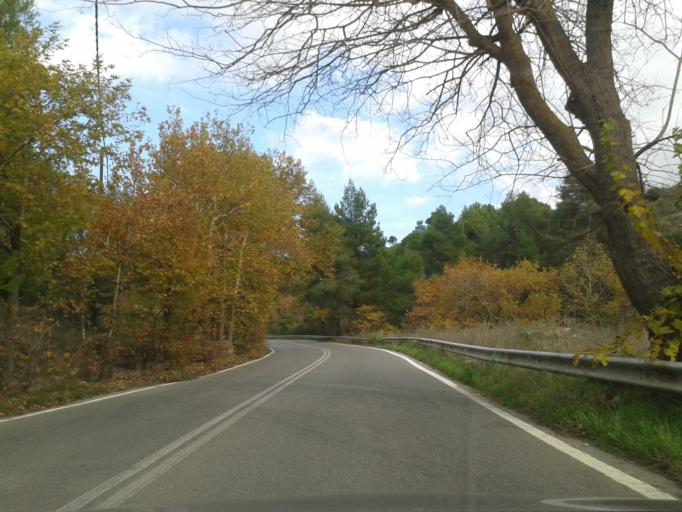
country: GR
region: Attica
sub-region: Nomarchia Anatolikis Attikis
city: Varnavas
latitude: 38.2147
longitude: 23.9125
